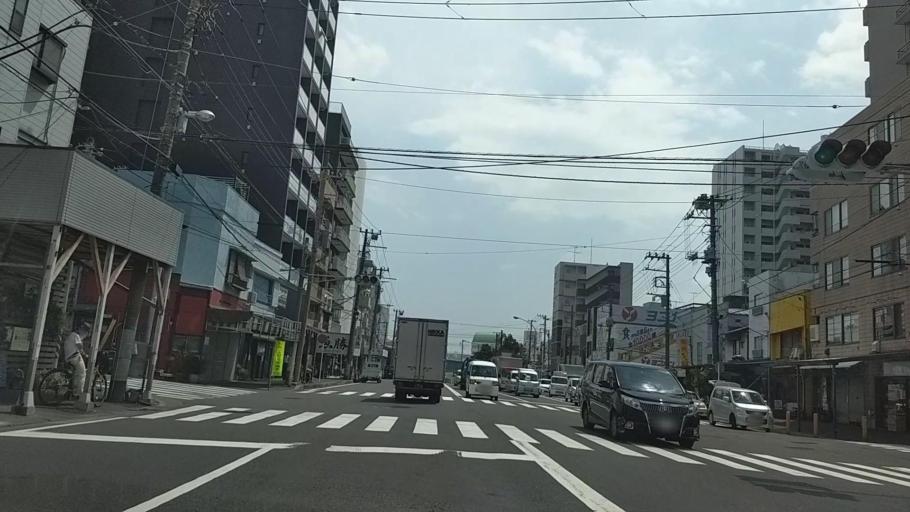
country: JP
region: Kanagawa
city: Yokohama
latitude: 35.4705
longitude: 139.6329
